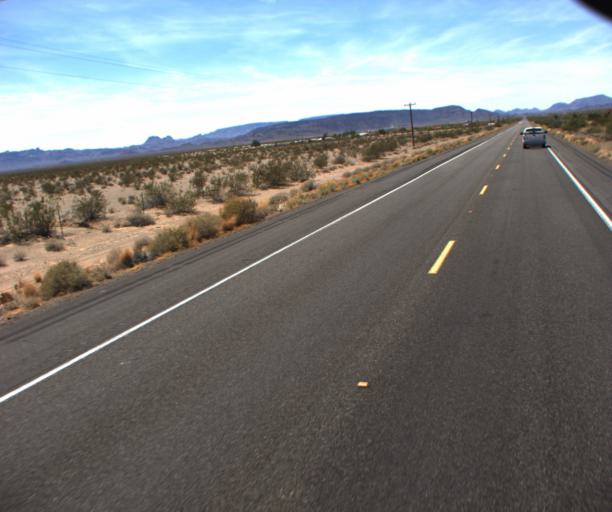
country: US
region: Arizona
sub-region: La Paz County
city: Salome
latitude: 33.7096
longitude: -113.8134
